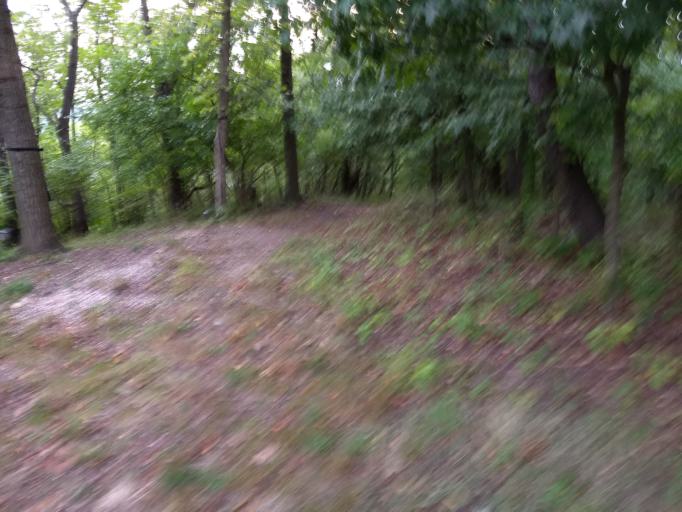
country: US
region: Pennsylvania
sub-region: Allegheny County
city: Green Tree
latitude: 40.4364
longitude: -80.0299
